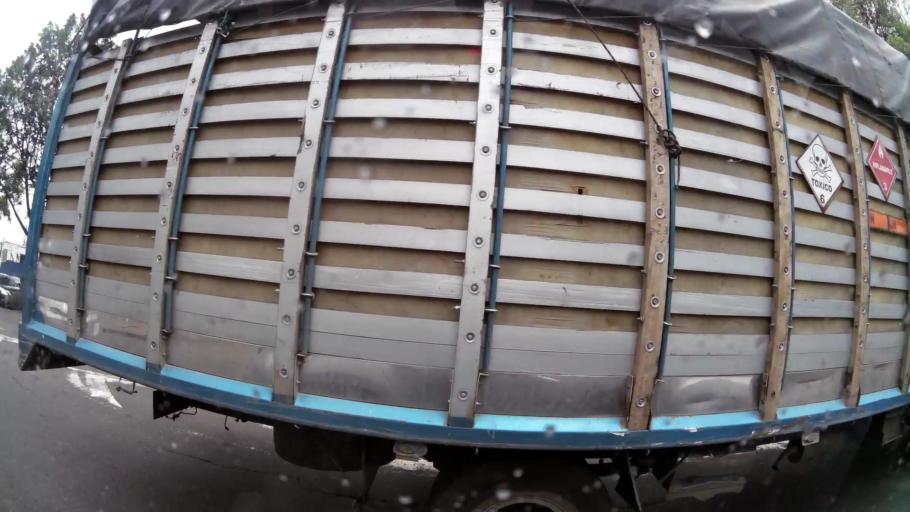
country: CO
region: Bogota D.C.
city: Bogota
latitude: 4.6407
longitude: -74.1151
